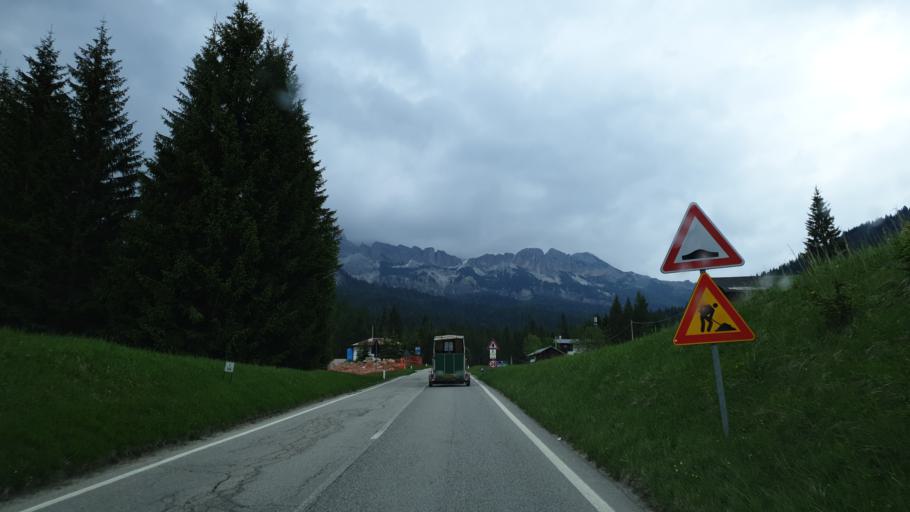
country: IT
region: Veneto
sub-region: Provincia di Belluno
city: San Vito
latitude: 46.5453
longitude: 12.2498
